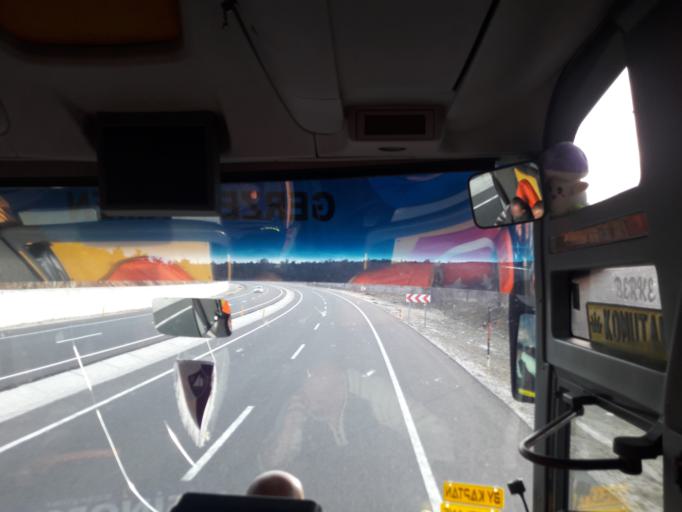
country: TR
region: Cankiri
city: Beloren
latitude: 40.8371
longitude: 33.5701
